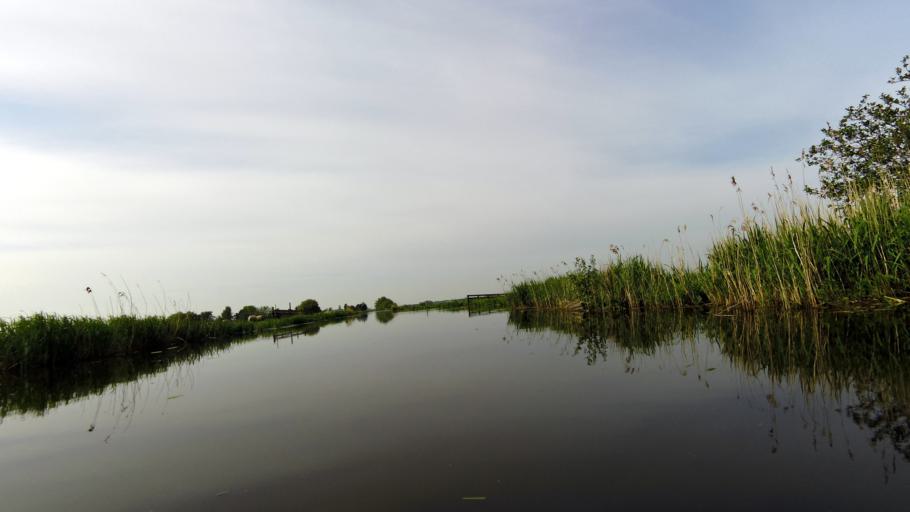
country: NL
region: South Holland
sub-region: Bodegraven-Reeuwijk
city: Reeuwijk
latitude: 52.0696
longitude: 4.7189
